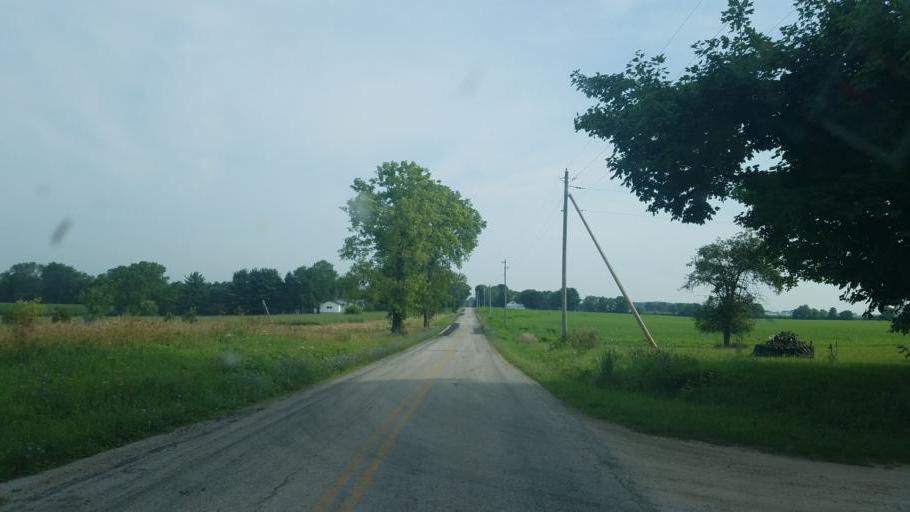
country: US
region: Ohio
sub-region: Delaware County
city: Ashley
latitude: 40.4858
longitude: -83.0537
